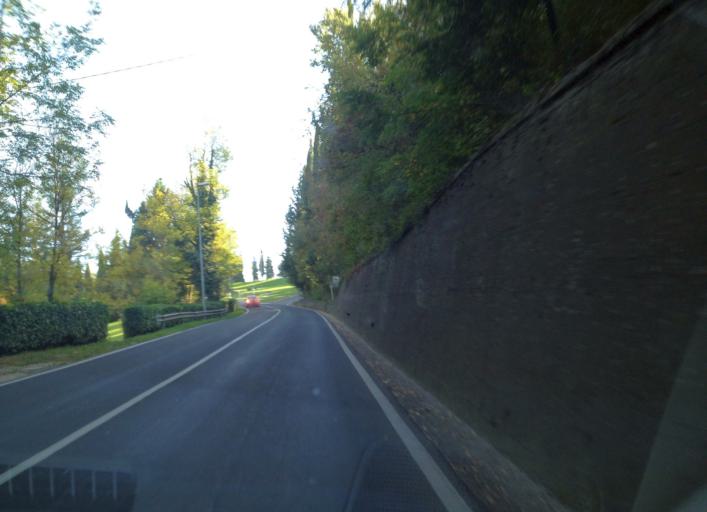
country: IT
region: Tuscany
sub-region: Provincia di Siena
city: Poggibonsi
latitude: 43.4601
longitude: 11.1472
